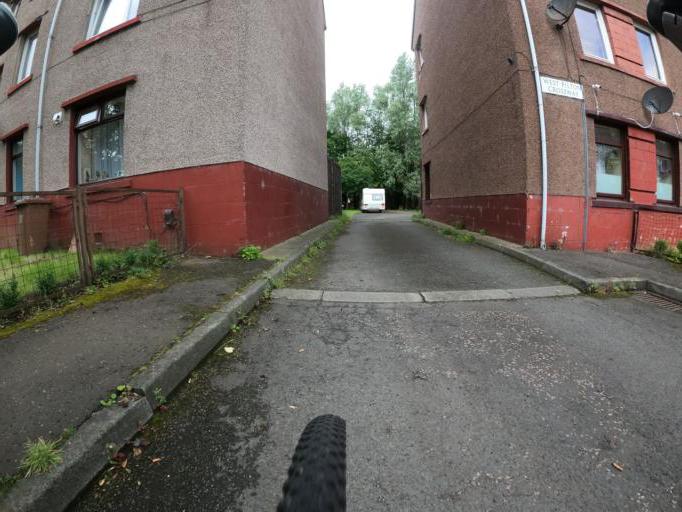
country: GB
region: Scotland
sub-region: Edinburgh
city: Edinburgh
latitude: 55.9721
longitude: -3.2501
